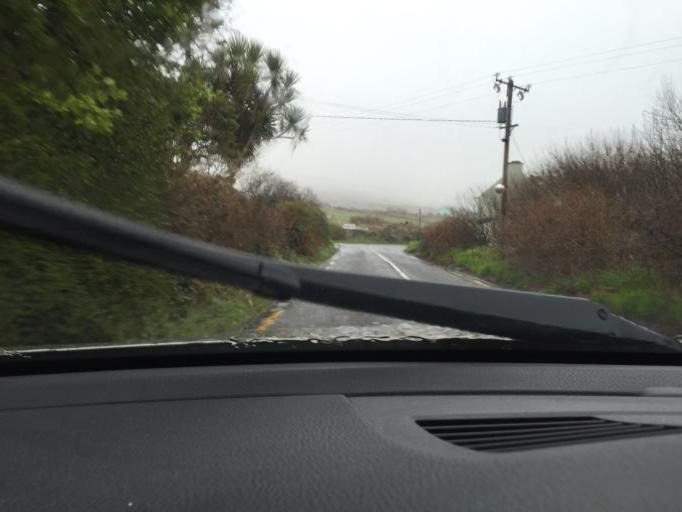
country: IE
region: Munster
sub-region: Ciarrai
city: Dingle
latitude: 52.1348
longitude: -10.3666
